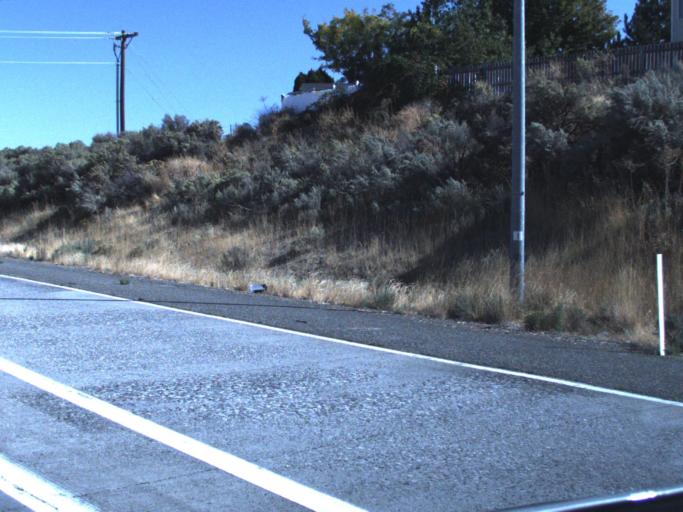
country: US
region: Washington
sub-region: Benton County
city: Richland
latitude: 46.2527
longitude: -119.3093
